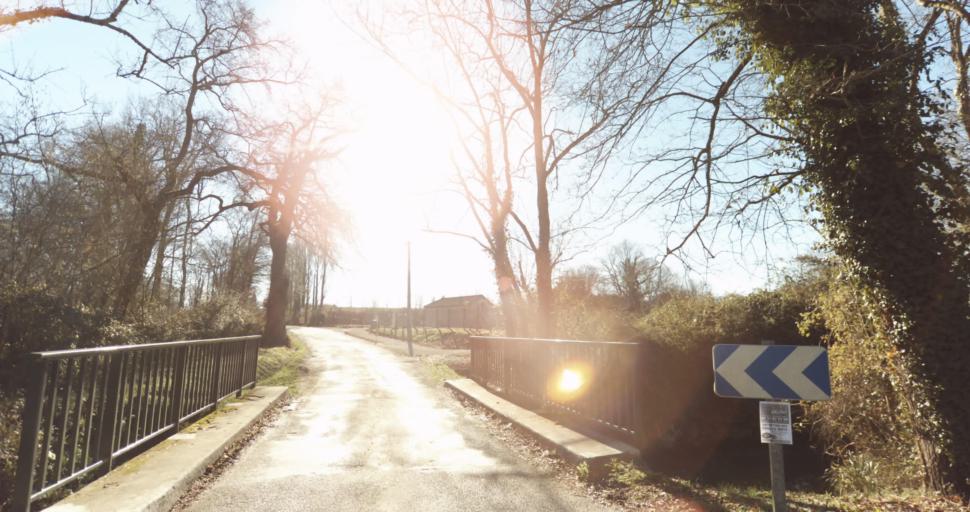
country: FR
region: Aquitaine
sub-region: Departement des Pyrenees-Atlantiques
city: Buros
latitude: 43.3314
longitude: -0.2997
